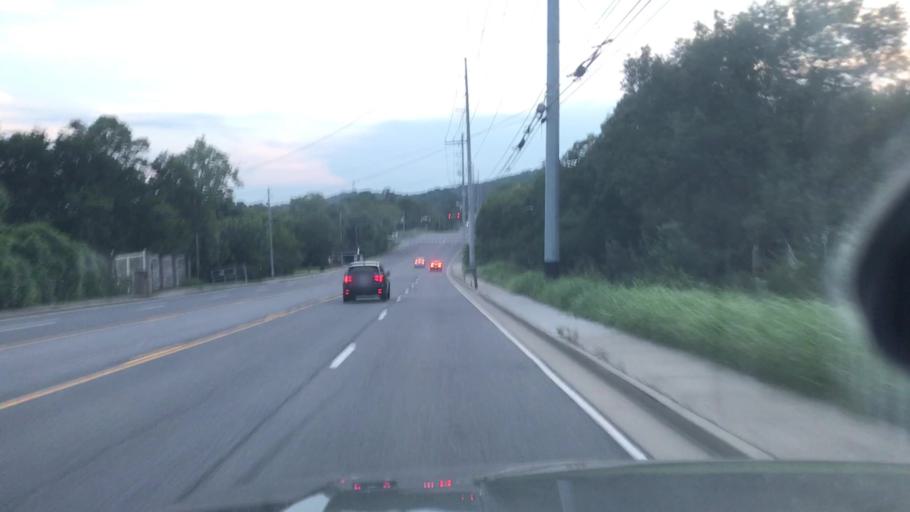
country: US
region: Tennessee
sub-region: Davidson County
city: Nashville
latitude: 36.2070
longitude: -86.8081
